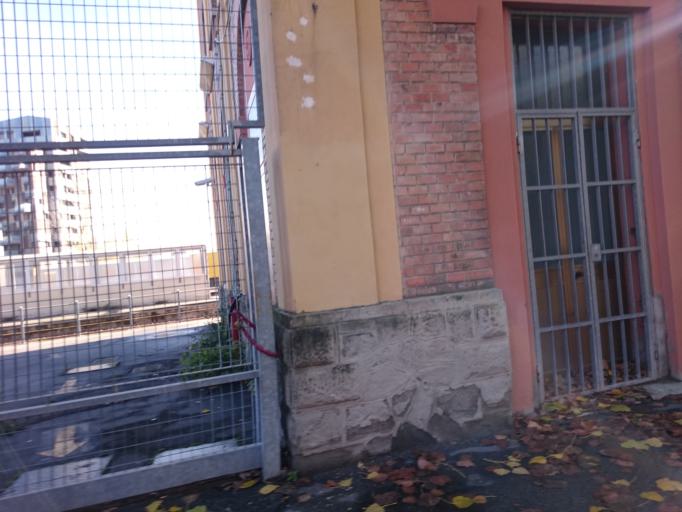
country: IT
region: Emilia-Romagna
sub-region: Provincia di Bologna
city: Bologna
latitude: 44.5107
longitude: 11.3359
